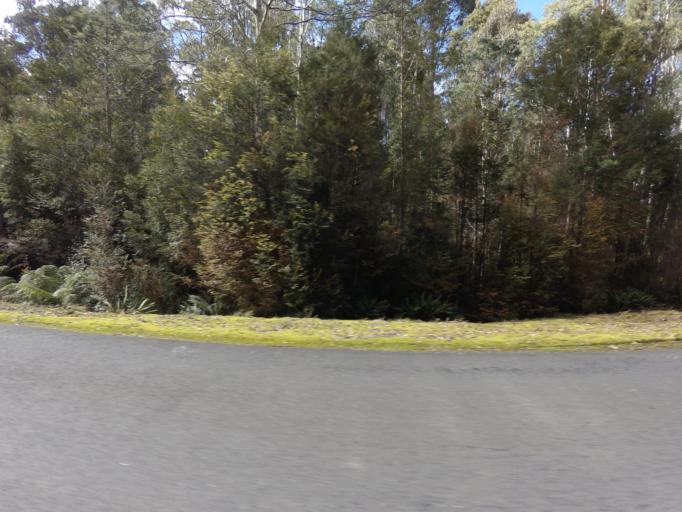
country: AU
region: Tasmania
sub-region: Huon Valley
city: Geeveston
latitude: -42.8189
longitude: 146.3320
